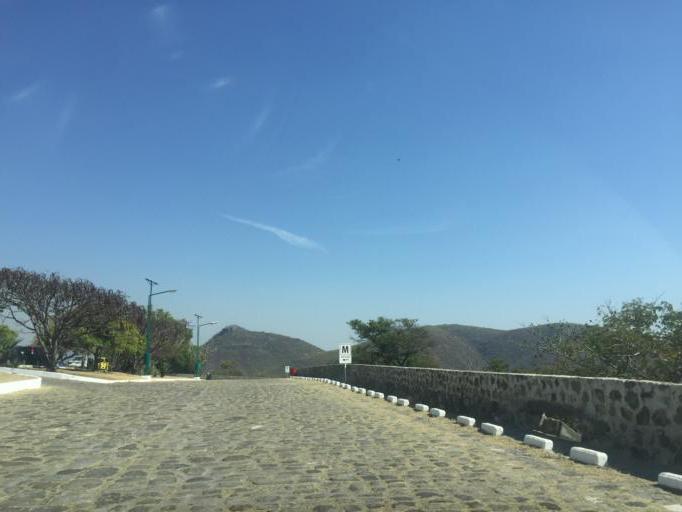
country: MX
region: Morelos
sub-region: Miacatlan
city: Xochicalco (Cirenio Longares)
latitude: 18.8019
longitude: -99.2910
